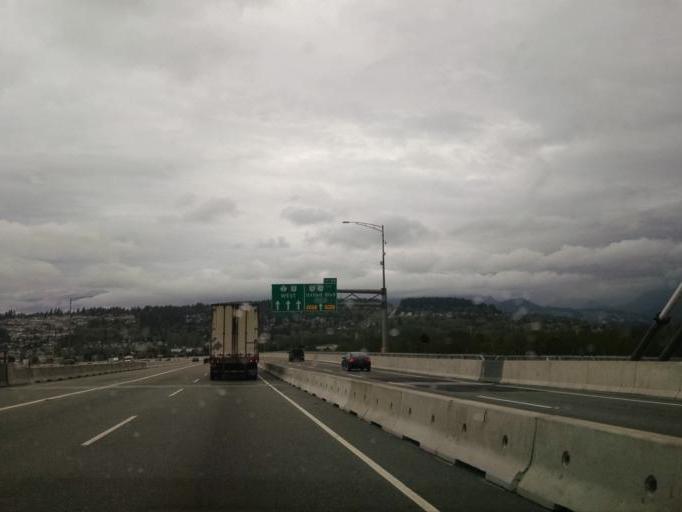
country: CA
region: British Columbia
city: Port Moody
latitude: 49.2210
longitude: -122.8135
